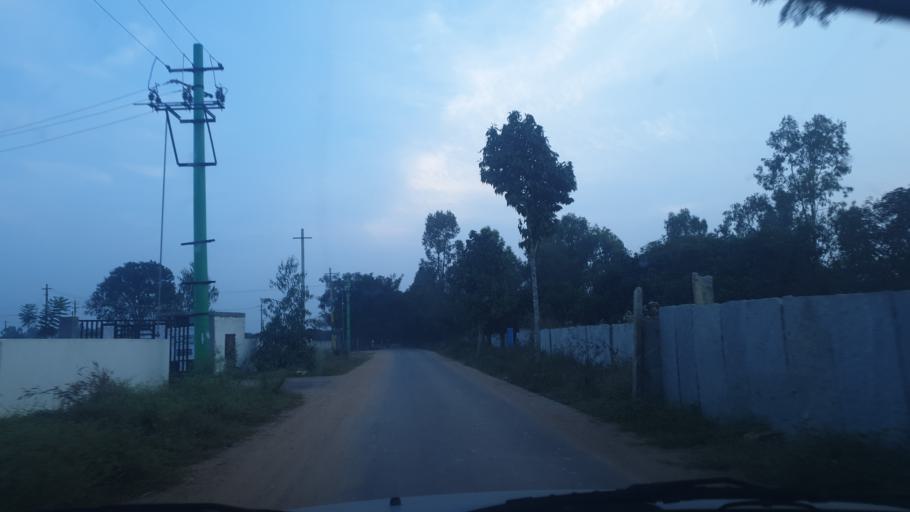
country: IN
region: Karnataka
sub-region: Bangalore Rural
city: Hoskote
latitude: 13.0850
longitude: 77.7017
